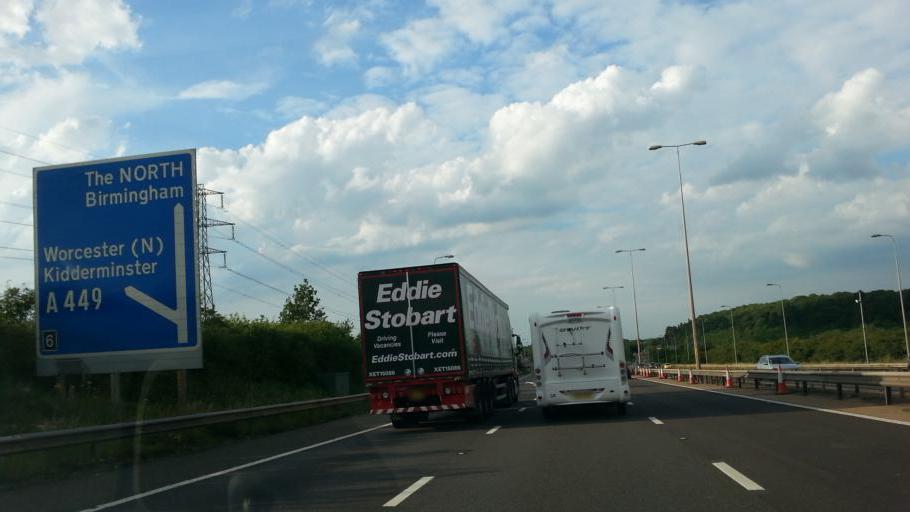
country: GB
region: England
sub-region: Worcestershire
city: Fernhill Heath
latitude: 52.2063
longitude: -2.1611
